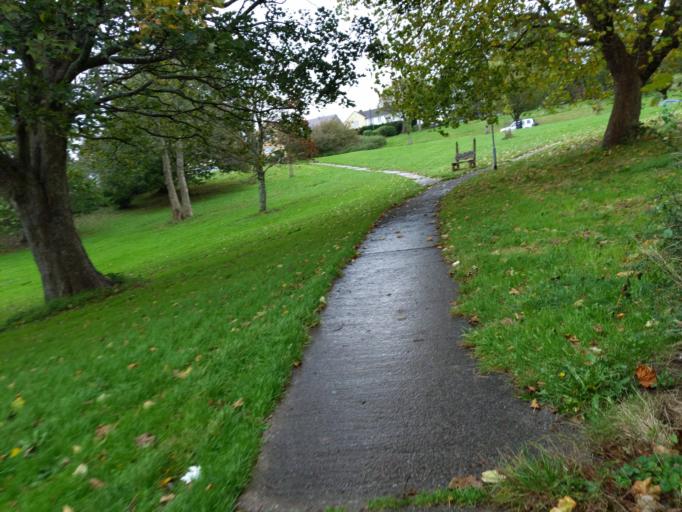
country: GB
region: England
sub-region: Plymouth
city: Plymouth
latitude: 50.4154
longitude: -4.1437
